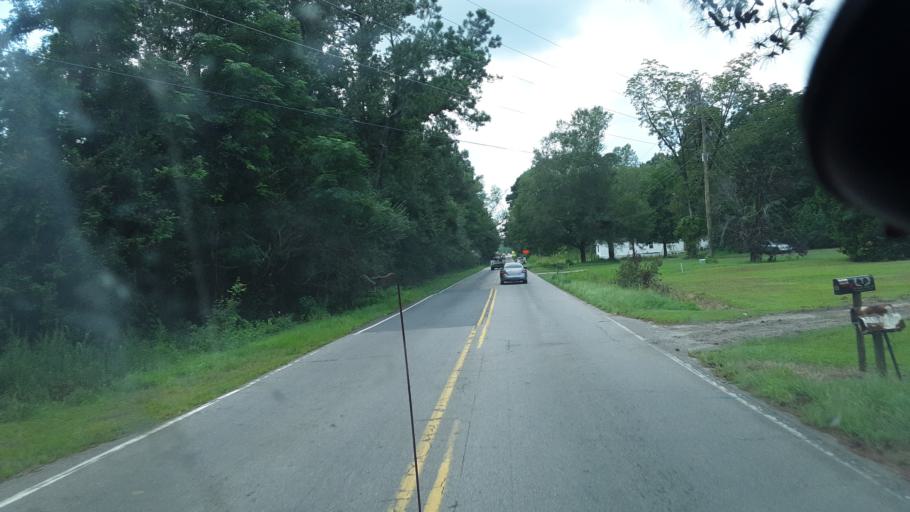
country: US
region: South Carolina
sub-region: Williamsburg County
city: Andrews
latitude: 33.3669
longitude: -79.4535
